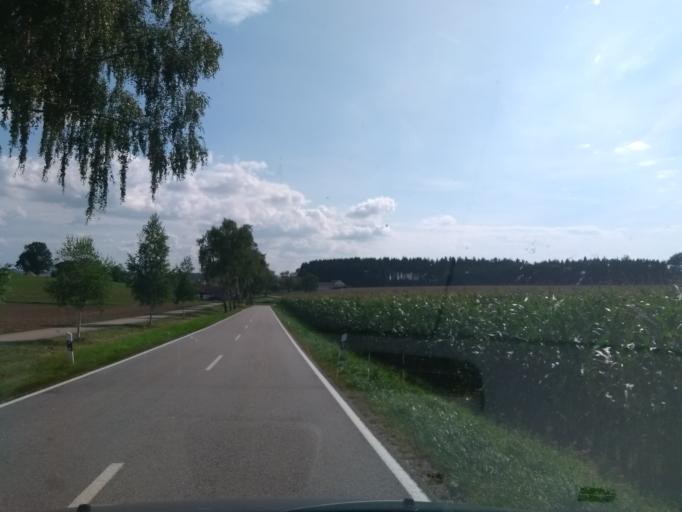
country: DE
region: Bavaria
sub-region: Upper Bavaria
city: Schwabhausen
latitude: 48.3988
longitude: 11.3484
